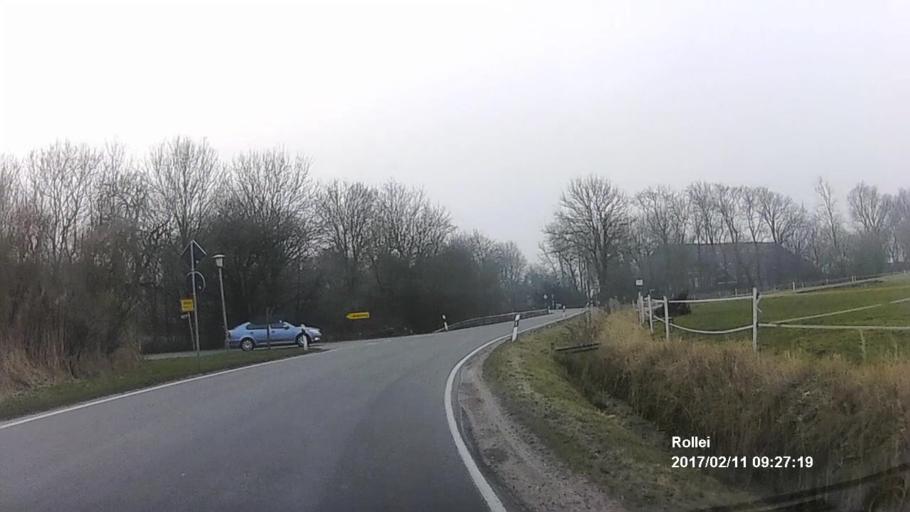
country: DE
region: Lower Saxony
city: Hinte
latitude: 53.4531
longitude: 7.1530
